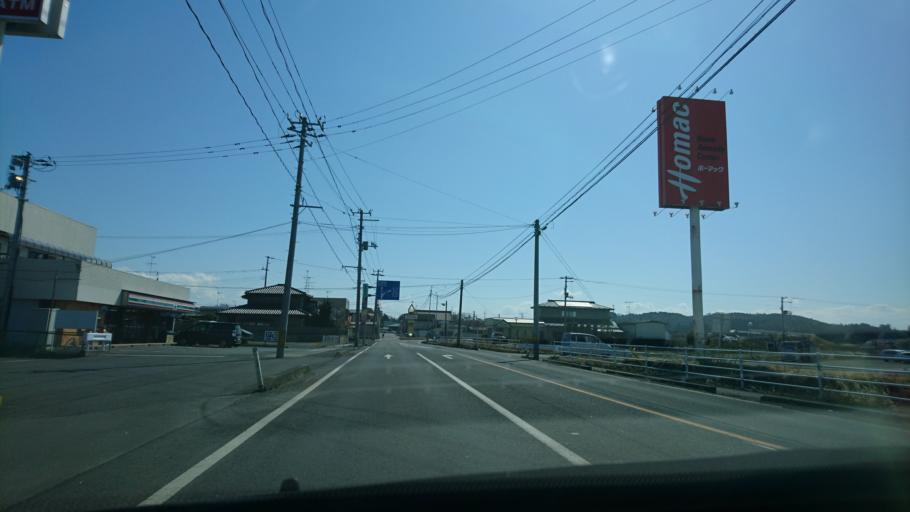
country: JP
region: Iwate
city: Ichinoseki
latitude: 38.7695
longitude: 141.1550
